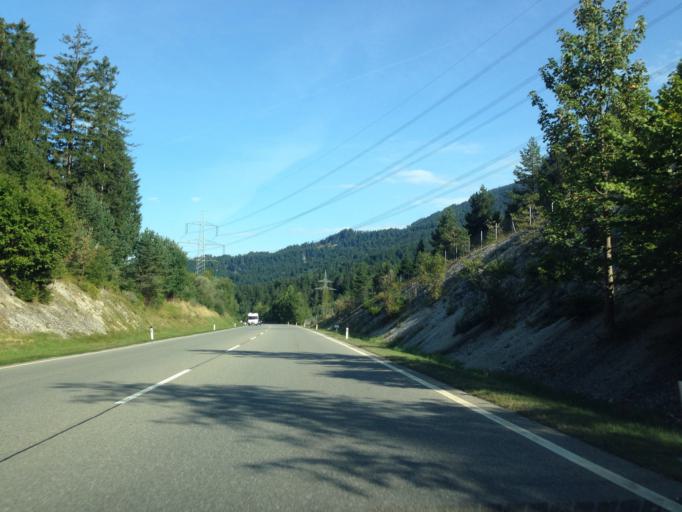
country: AT
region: Tyrol
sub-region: Politischer Bezirk Reutte
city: Pflach
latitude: 47.5083
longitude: 10.7339
